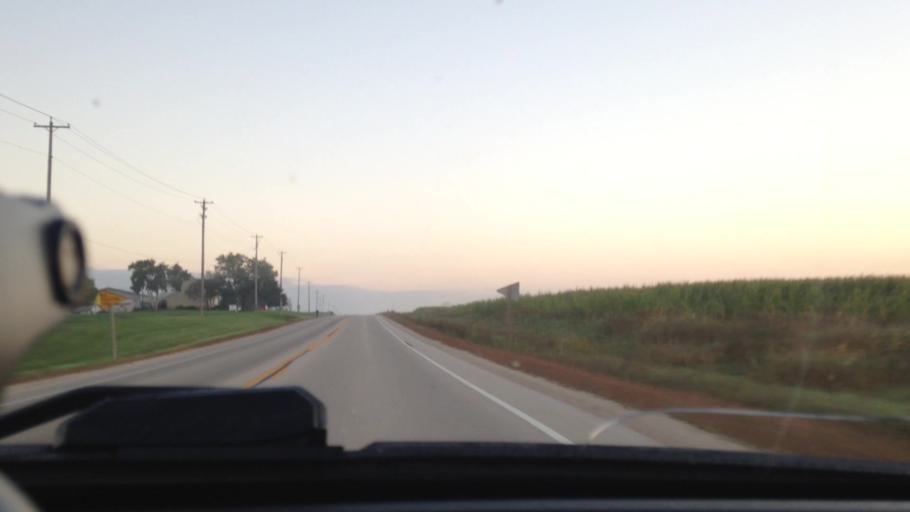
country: US
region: Wisconsin
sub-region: Dodge County
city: Lomira
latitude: 43.5711
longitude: -88.4499
